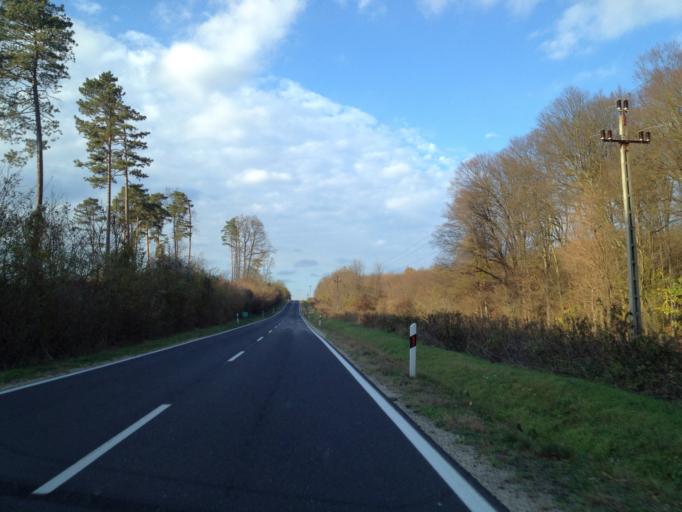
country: HU
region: Gyor-Moson-Sopron
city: Bakonyszentlaszlo
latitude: 47.4062
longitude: 17.8541
